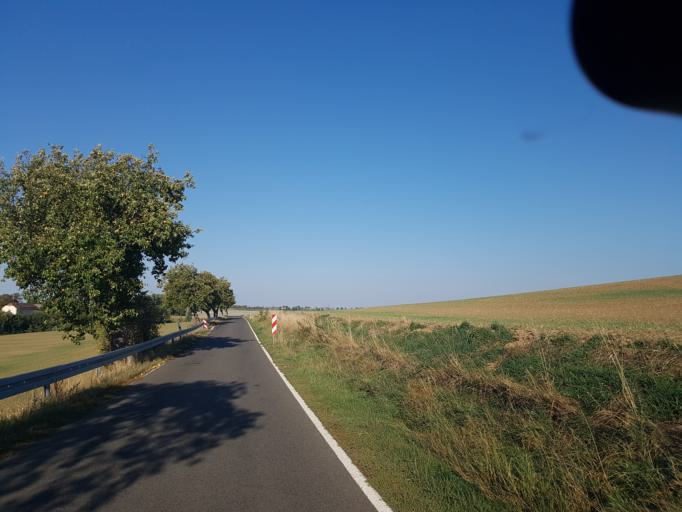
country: DE
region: Saxony
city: Ostrau
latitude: 51.1929
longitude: 13.1171
